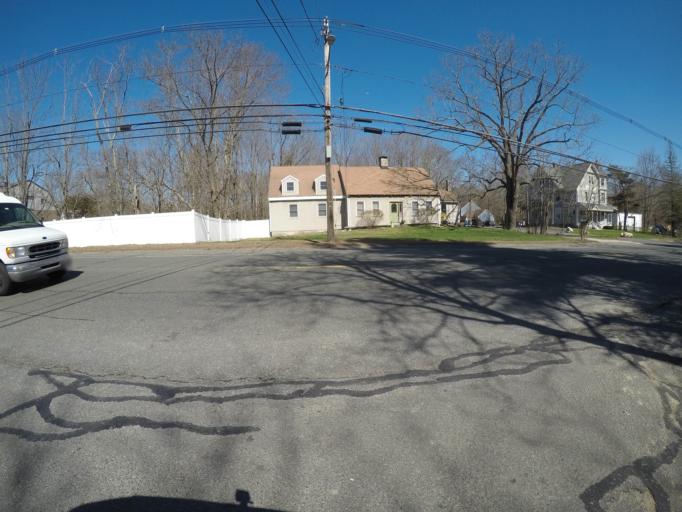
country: US
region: Massachusetts
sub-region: Norfolk County
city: Stoughton
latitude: 42.0834
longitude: -71.0905
